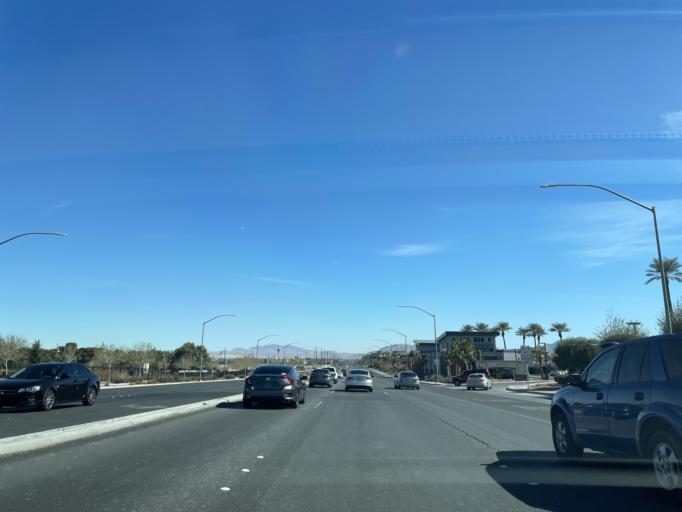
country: US
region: Nevada
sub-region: Clark County
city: North Las Vegas
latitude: 36.2394
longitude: -115.1527
